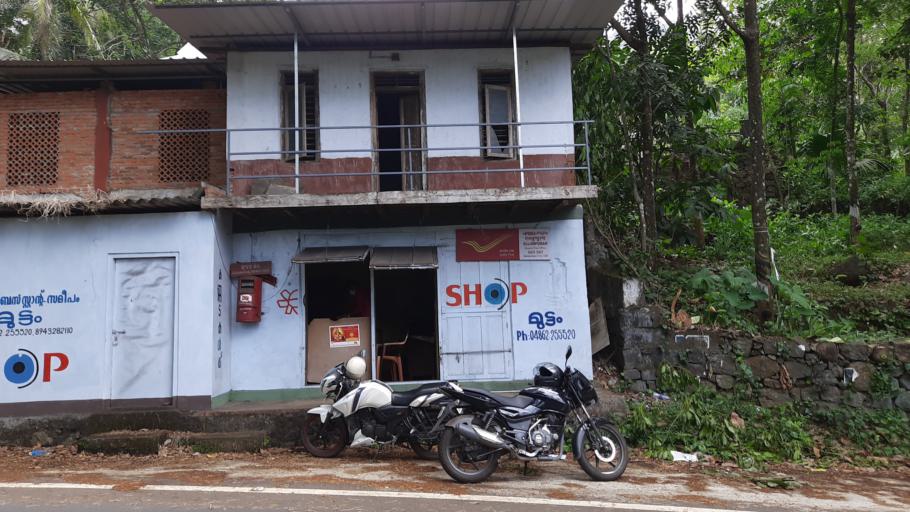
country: IN
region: Kerala
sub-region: Kottayam
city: Lalam
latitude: 9.8136
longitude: 76.7473
